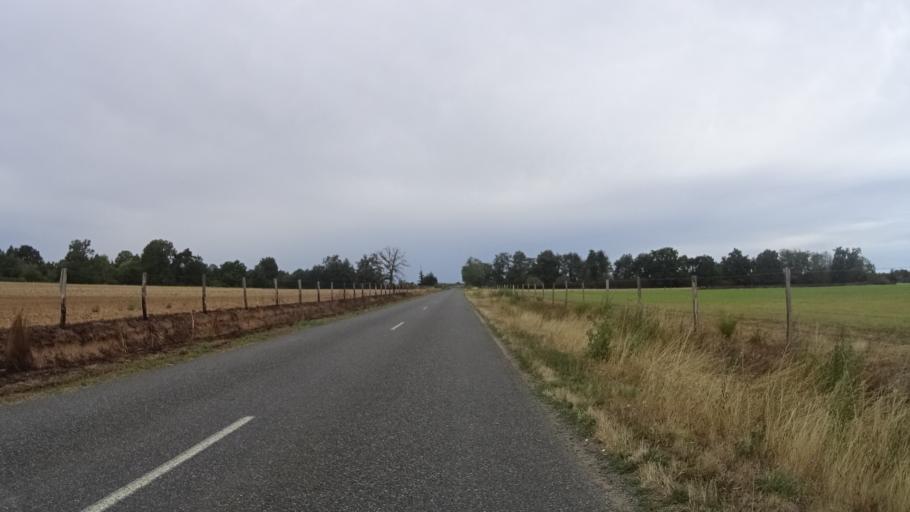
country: FR
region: Bourgogne
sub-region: Departement de la Nievre
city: Lucenay-les-Aix
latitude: 46.7719
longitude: 3.5513
